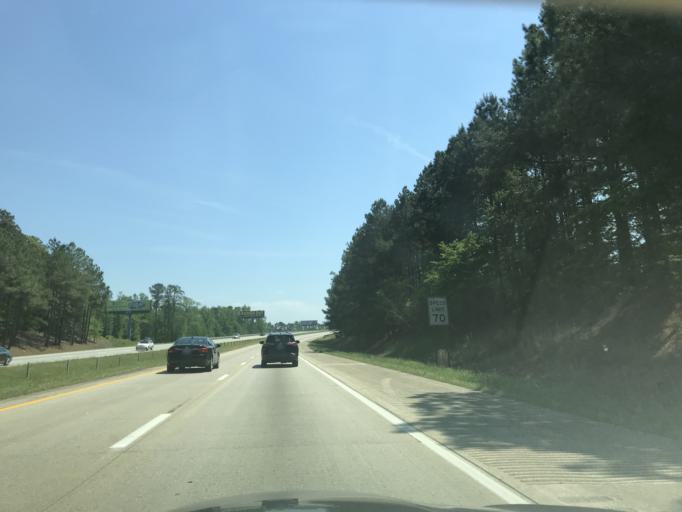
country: US
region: North Carolina
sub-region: Johnston County
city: Benson
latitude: 35.4133
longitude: -78.5255
